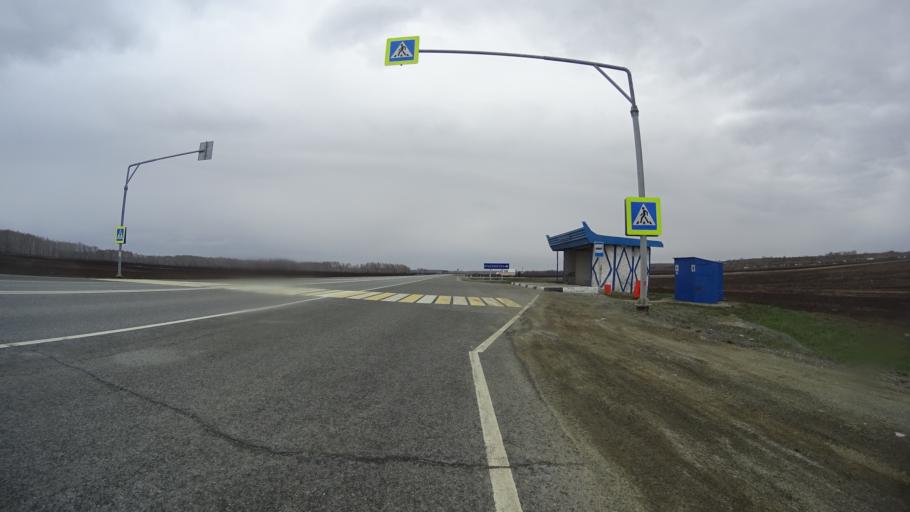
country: RU
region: Chelyabinsk
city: Krasnogorskiy
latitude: 54.5819
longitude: 61.2911
